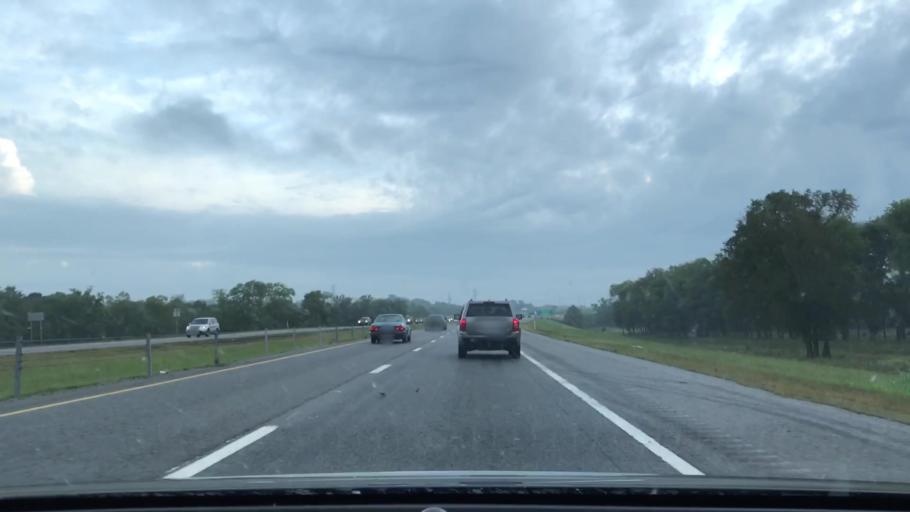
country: US
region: Tennessee
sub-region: Sumner County
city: Shackle Island
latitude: 36.3521
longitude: -86.5411
